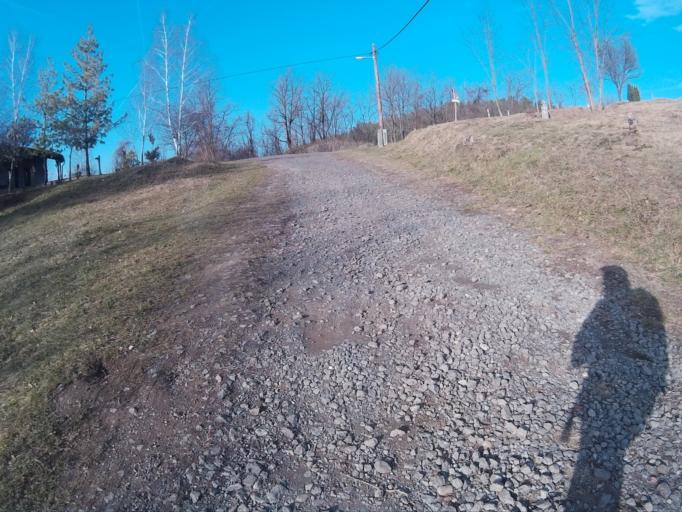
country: HU
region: Nograd
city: Bercel
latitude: 47.9492
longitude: 19.4438
